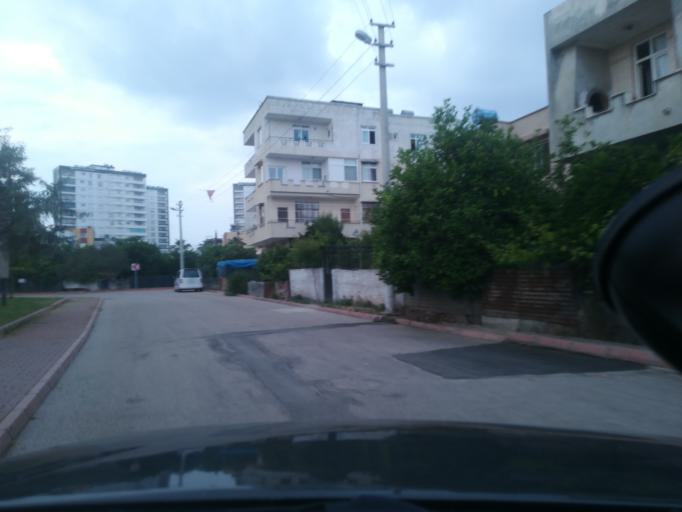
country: TR
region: Adana
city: Seyhan
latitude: 37.0195
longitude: 35.2709
